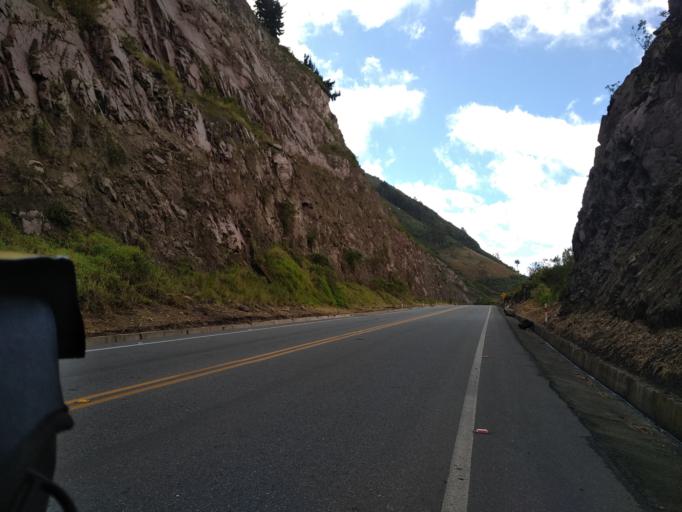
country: EC
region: Tungurahua
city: Banos
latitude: -1.4833
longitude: -78.5186
